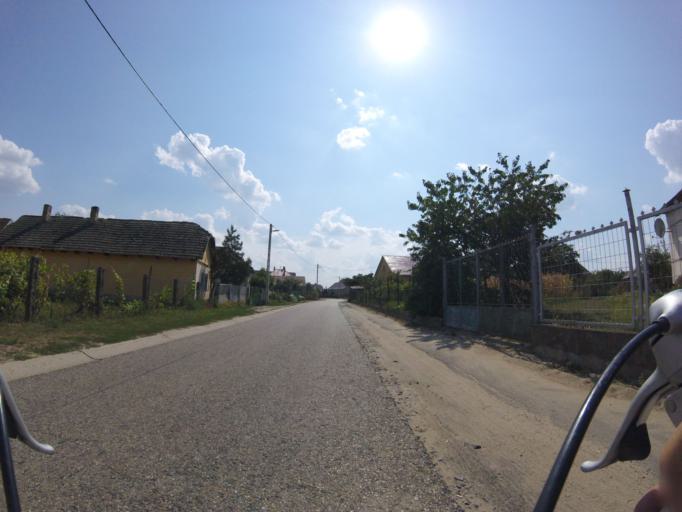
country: HU
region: Szabolcs-Szatmar-Bereg
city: Nyirtass
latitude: 48.1142
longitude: 22.0247
